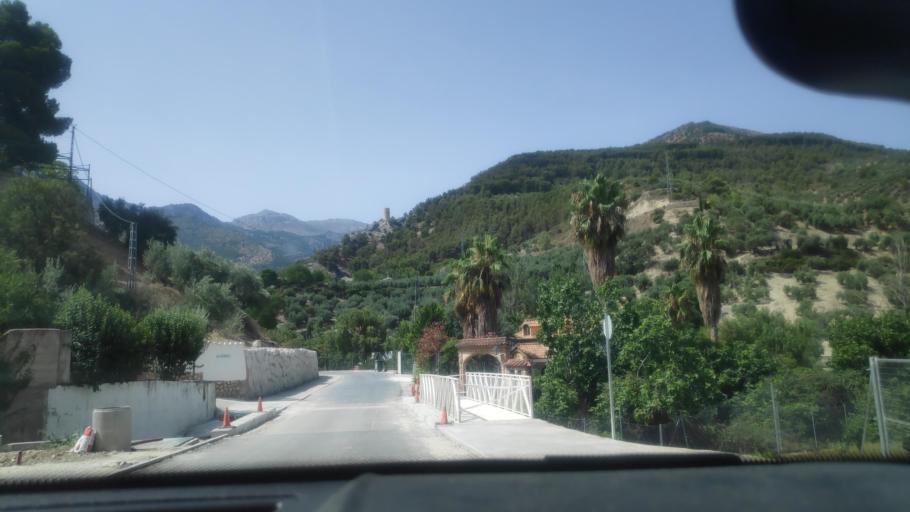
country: ES
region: Andalusia
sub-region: Provincia de Jaen
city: Jodar
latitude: 37.7946
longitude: -3.4068
